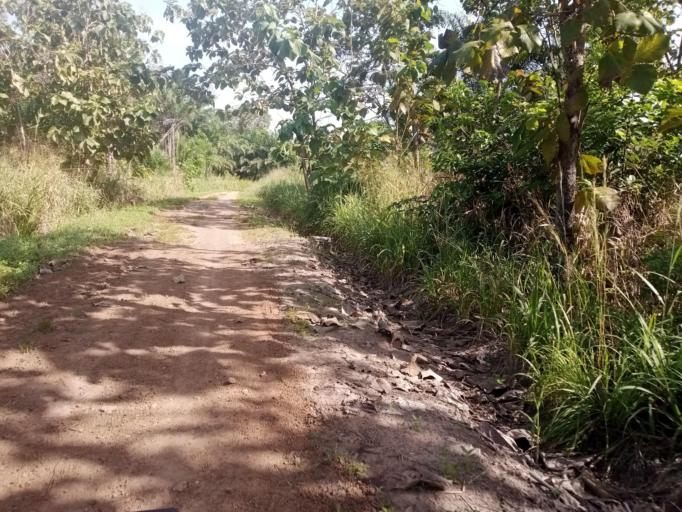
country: TG
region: Maritime
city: Tsevie
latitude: 6.6610
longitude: 0.9721
